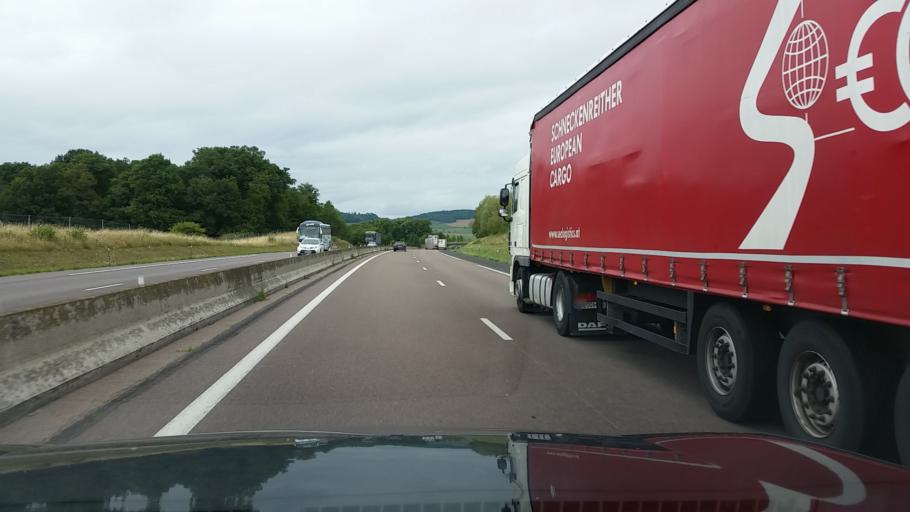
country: FR
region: Lorraine
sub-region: Departement des Vosges
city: Chatenois
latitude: 48.3411
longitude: 5.8534
